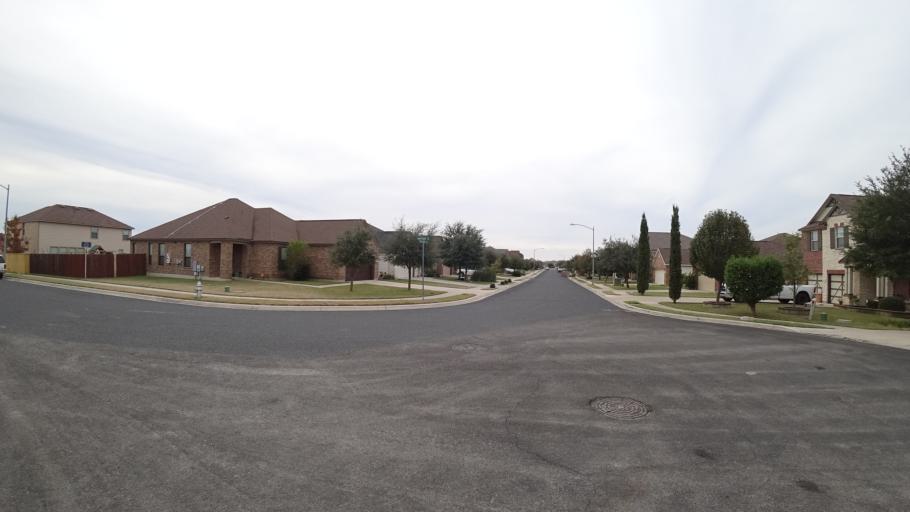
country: US
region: Texas
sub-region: Travis County
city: Onion Creek
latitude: 30.1539
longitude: -97.7478
